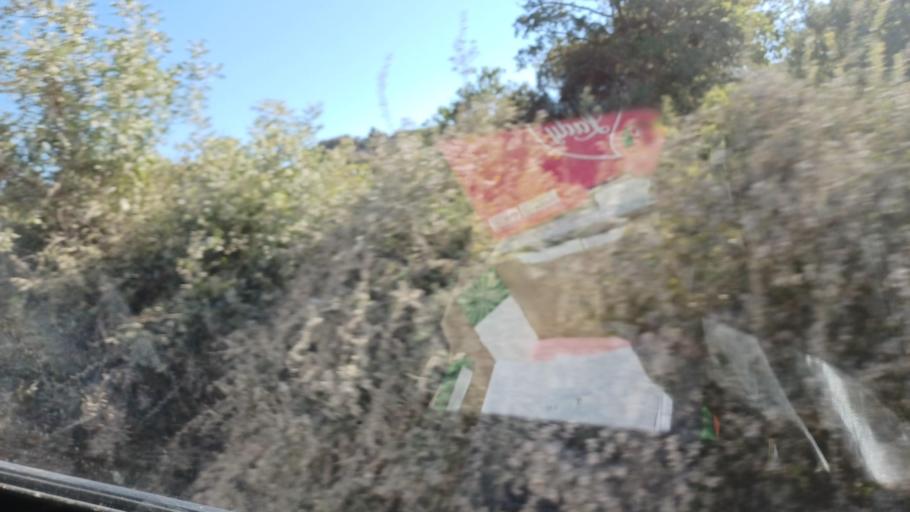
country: CY
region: Pafos
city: Polis
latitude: 34.9594
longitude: 32.4290
